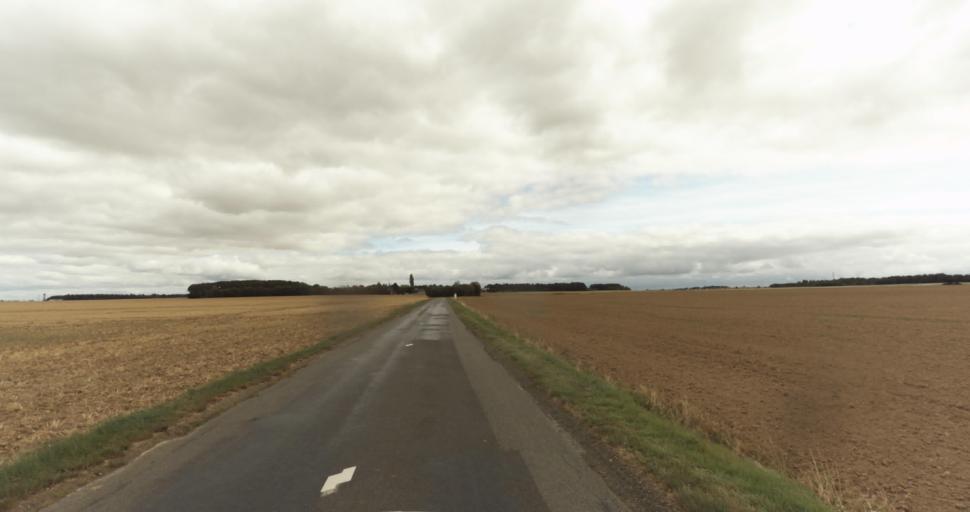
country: FR
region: Haute-Normandie
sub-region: Departement de l'Eure
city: Arnieres-sur-Iton
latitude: 48.9226
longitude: 1.1768
